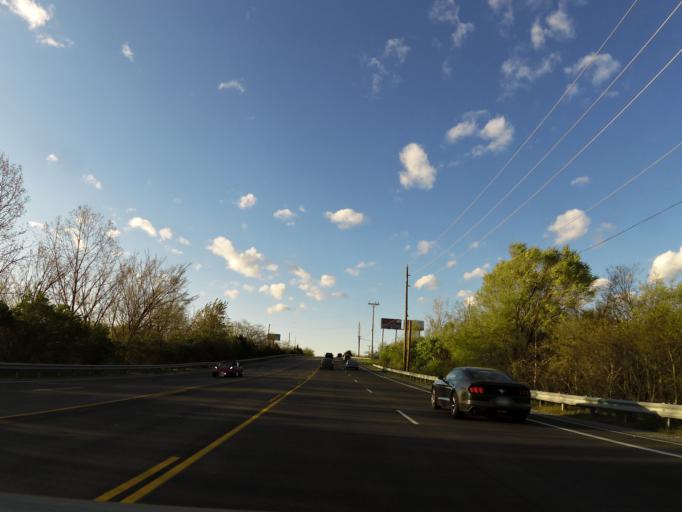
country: US
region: Tennessee
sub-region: Davidson County
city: Goodlettsville
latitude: 36.2861
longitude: -86.6928
